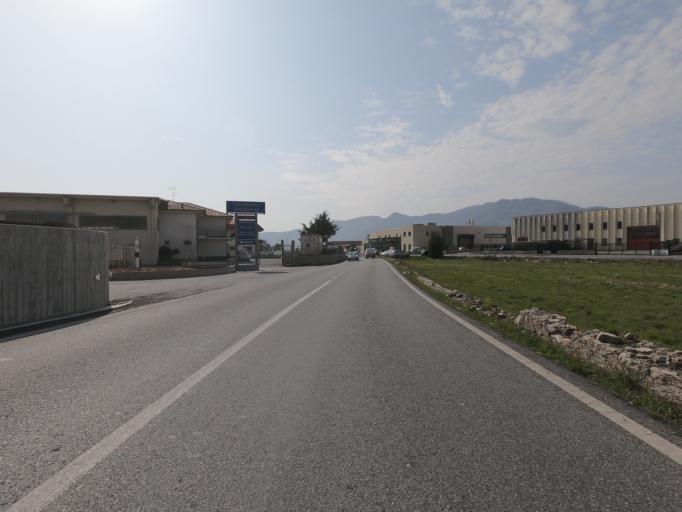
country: IT
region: Liguria
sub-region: Provincia di Savona
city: Cisano
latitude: 44.0726
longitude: 8.1669
